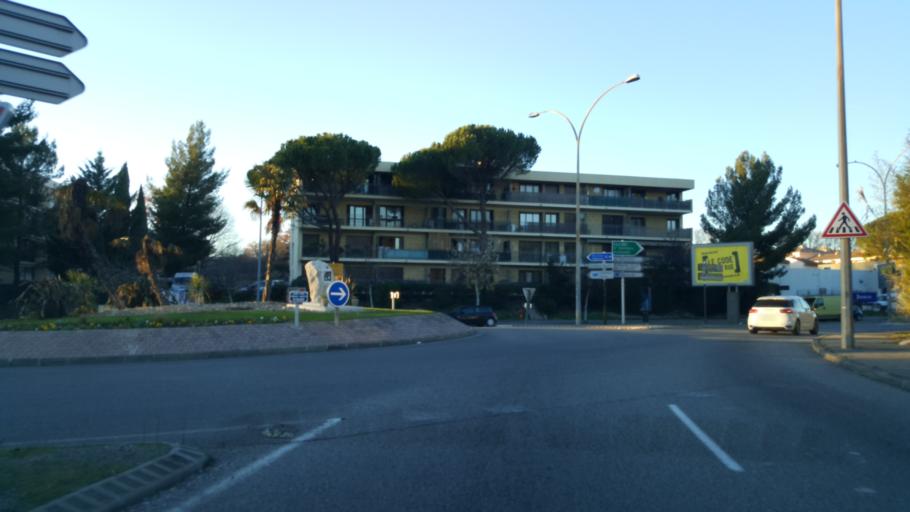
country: FR
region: Provence-Alpes-Cote d'Azur
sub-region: Departement des Bouches-du-Rhone
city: Aix-en-Provence
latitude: 43.5149
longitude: 5.4664
